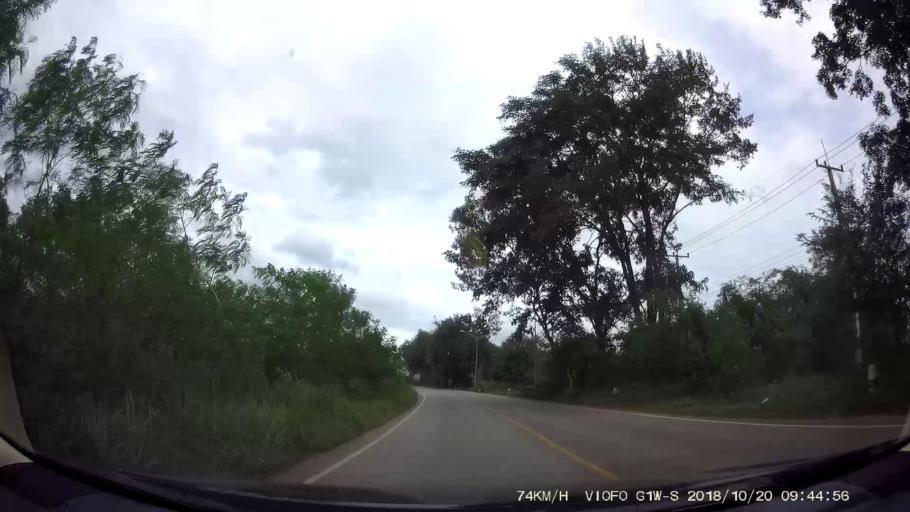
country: TH
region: Chaiyaphum
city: Khon San
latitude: 16.4882
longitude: 101.9414
